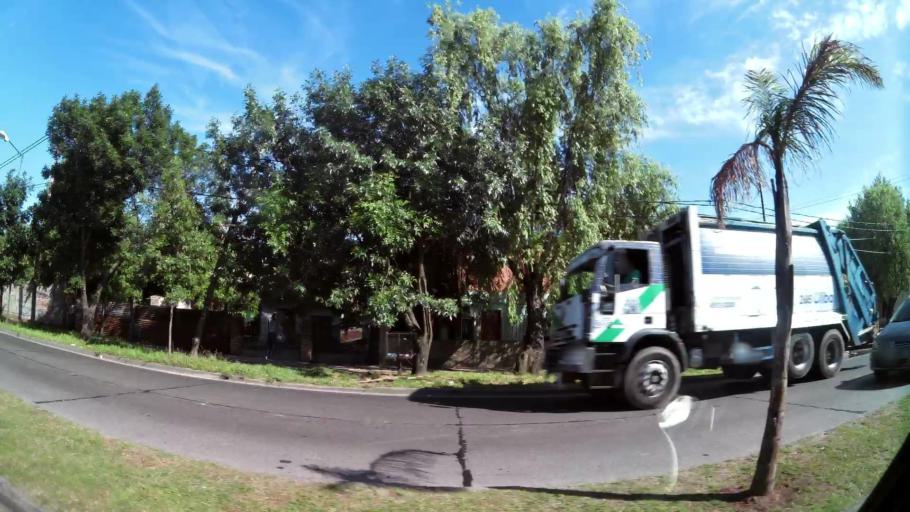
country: AR
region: Buenos Aires
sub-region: Partido de Tigre
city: Tigre
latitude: -34.4786
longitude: -58.5816
